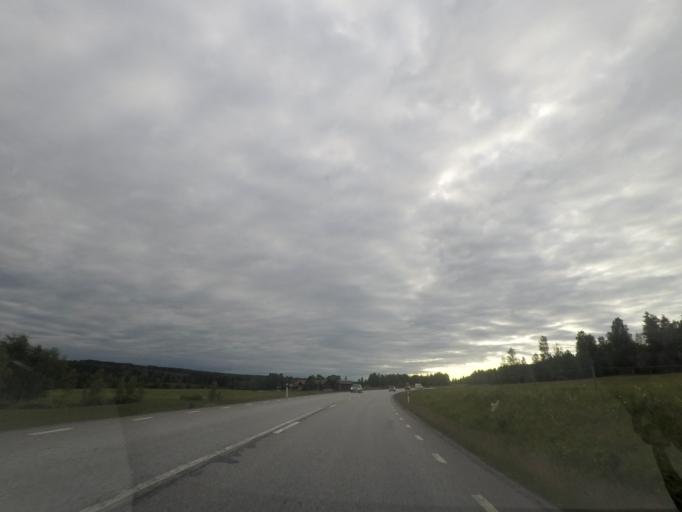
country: SE
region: OErebro
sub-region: Ljusnarsbergs Kommun
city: Kopparberg
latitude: 59.8341
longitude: 15.1018
